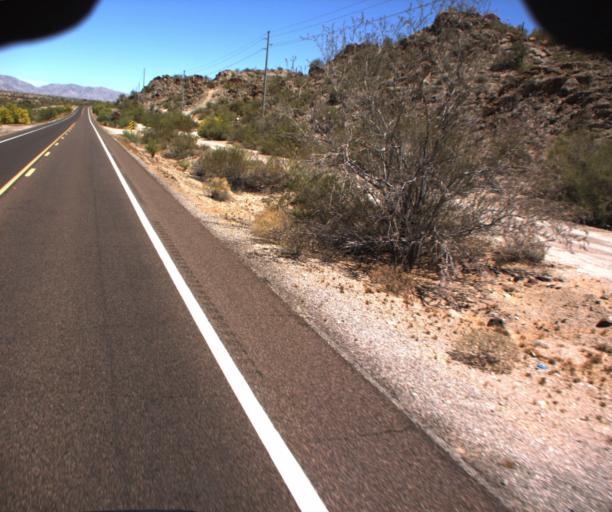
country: US
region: Arizona
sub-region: La Paz County
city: Salome
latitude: 33.7440
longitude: -113.6739
